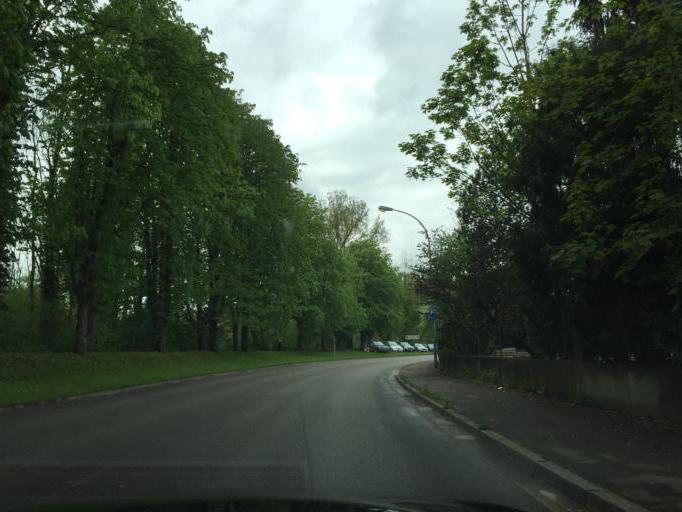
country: DE
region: Bavaria
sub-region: Swabia
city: Dillingen an der Donau
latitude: 48.5722
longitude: 10.4902
